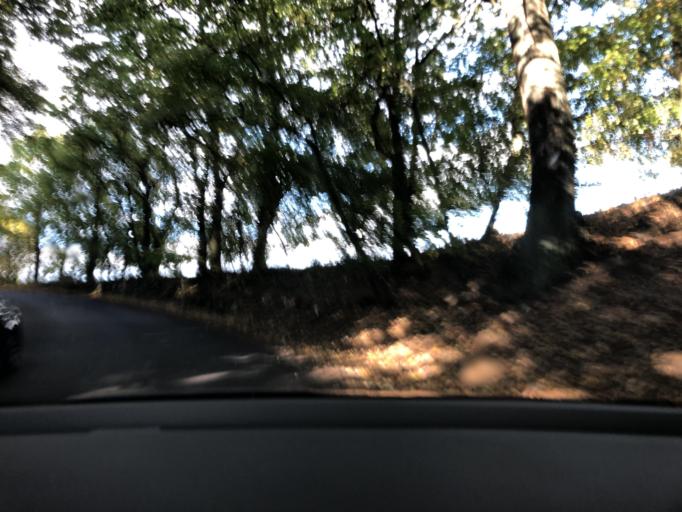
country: CZ
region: Ustecky
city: Zitenice
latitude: 50.5850
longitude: 14.1698
